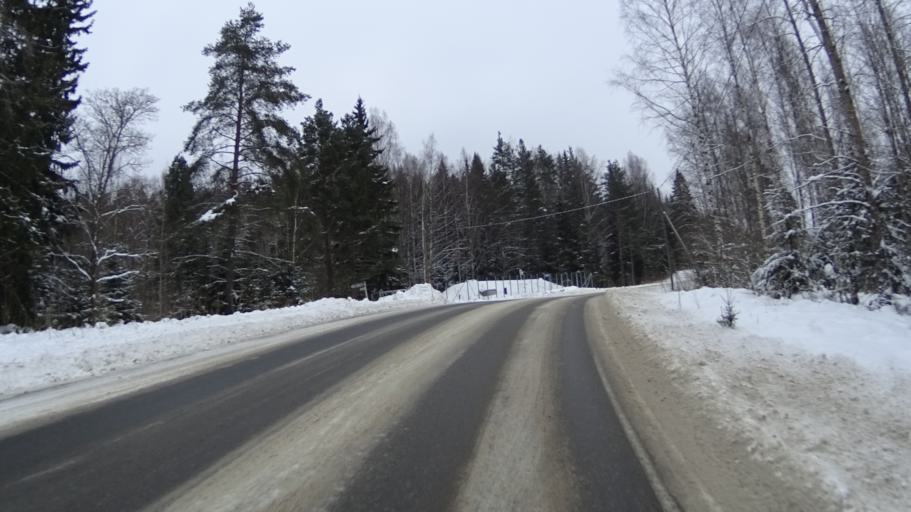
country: FI
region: Uusimaa
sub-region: Helsinki
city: Karkkila
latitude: 60.5095
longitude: 24.1497
